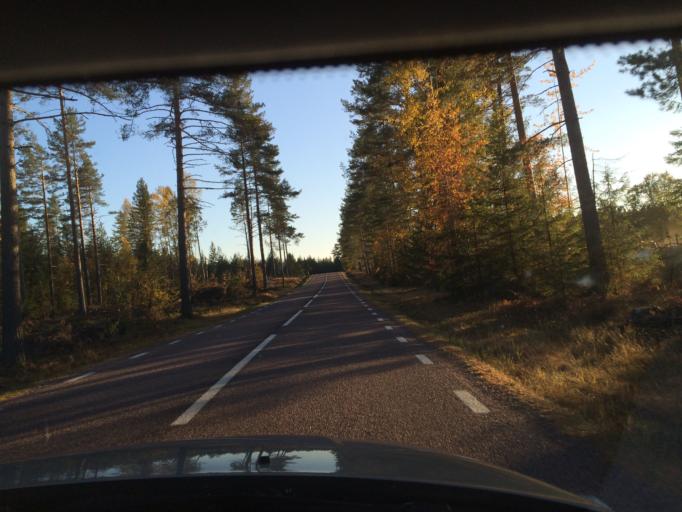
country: SE
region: Gaevleborg
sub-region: Sandvikens Kommun
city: Arsunda
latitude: 60.4816
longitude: 16.7183
